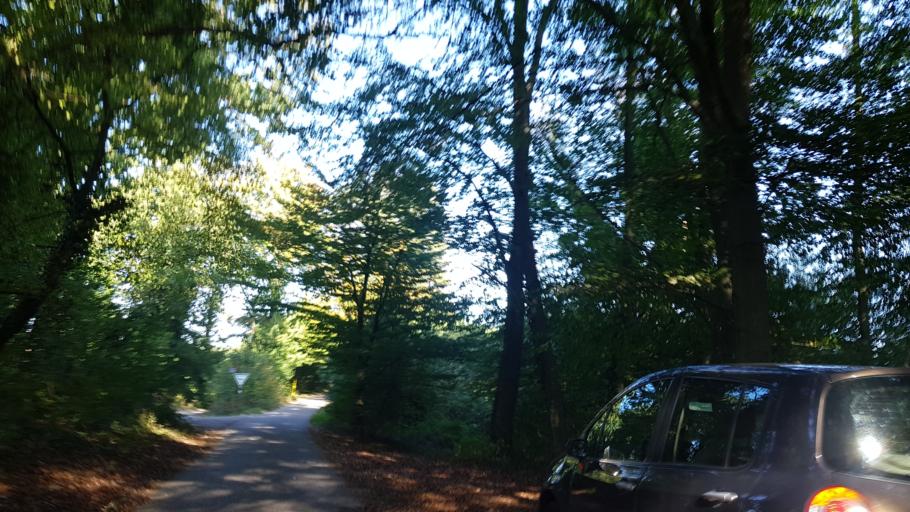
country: DE
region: North Rhine-Westphalia
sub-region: Regierungsbezirk Dusseldorf
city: Ratingen
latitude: 51.3710
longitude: 6.8198
